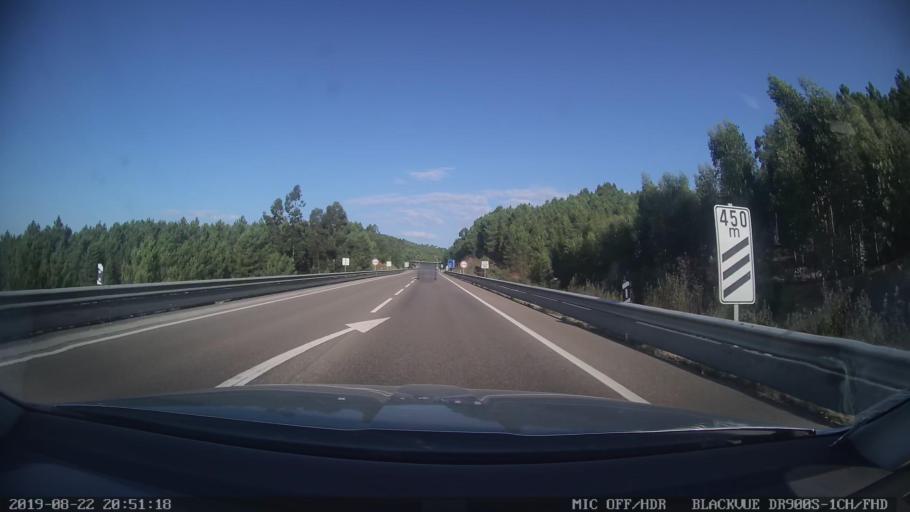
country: PT
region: Castelo Branco
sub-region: Proenca-A-Nova
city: Proenca-a-Nova
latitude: 39.7593
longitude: -7.9567
